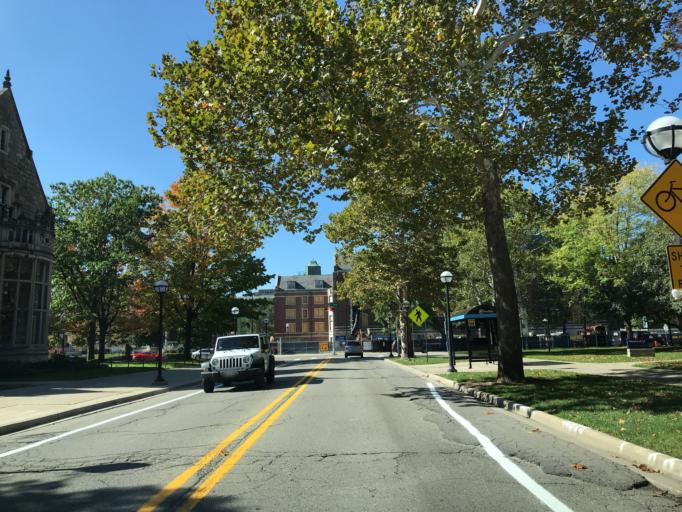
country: US
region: Michigan
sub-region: Washtenaw County
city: Ann Arbor
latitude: 42.2749
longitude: -83.7397
